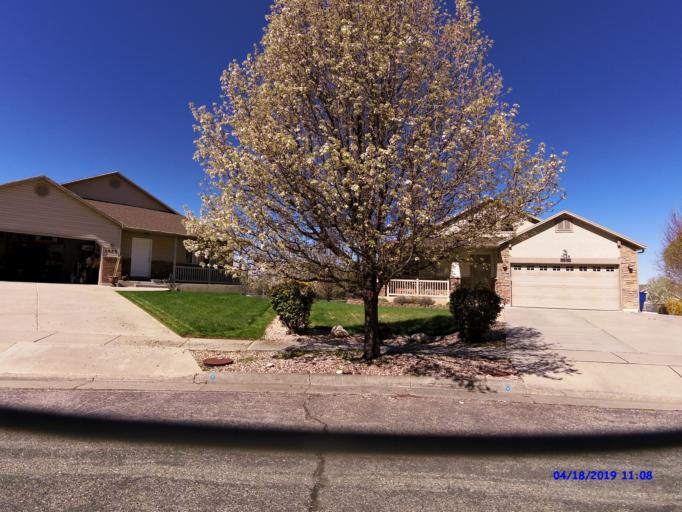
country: US
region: Utah
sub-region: Weber County
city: North Ogden
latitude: 41.2845
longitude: -111.9519
